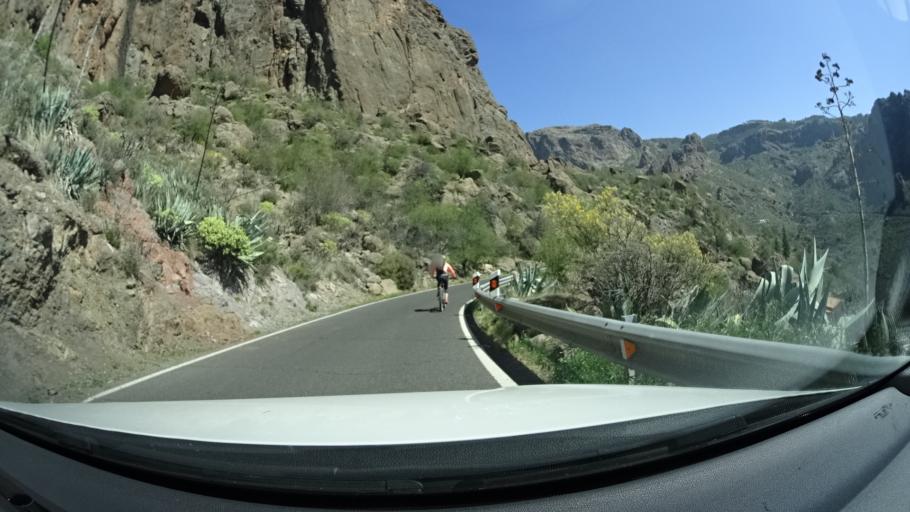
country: ES
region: Canary Islands
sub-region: Provincia de Las Palmas
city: Tejeda
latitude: 27.9557
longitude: -15.6176
